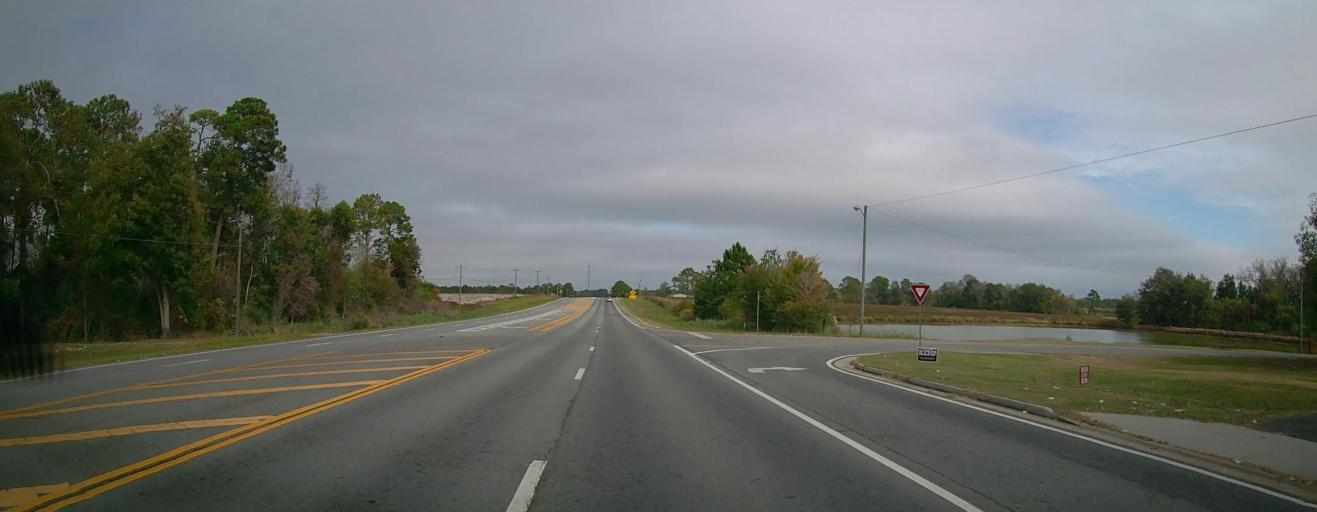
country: US
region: Georgia
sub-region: Tift County
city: Omega
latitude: 31.3747
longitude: -83.5654
